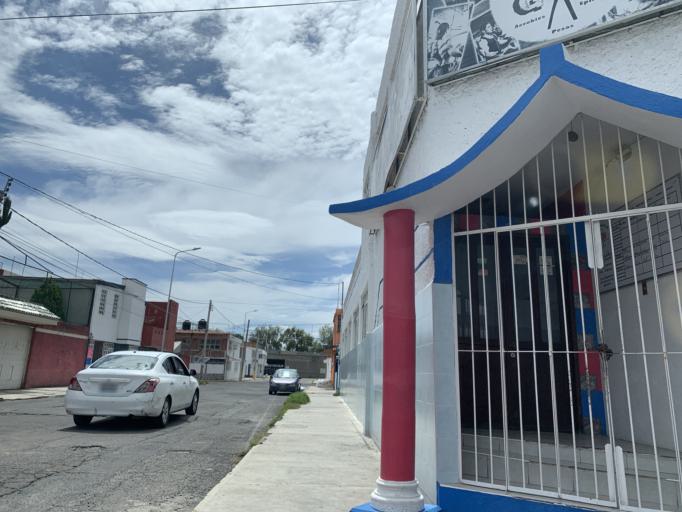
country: MX
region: Puebla
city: Puebla
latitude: 19.0633
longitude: -98.2071
